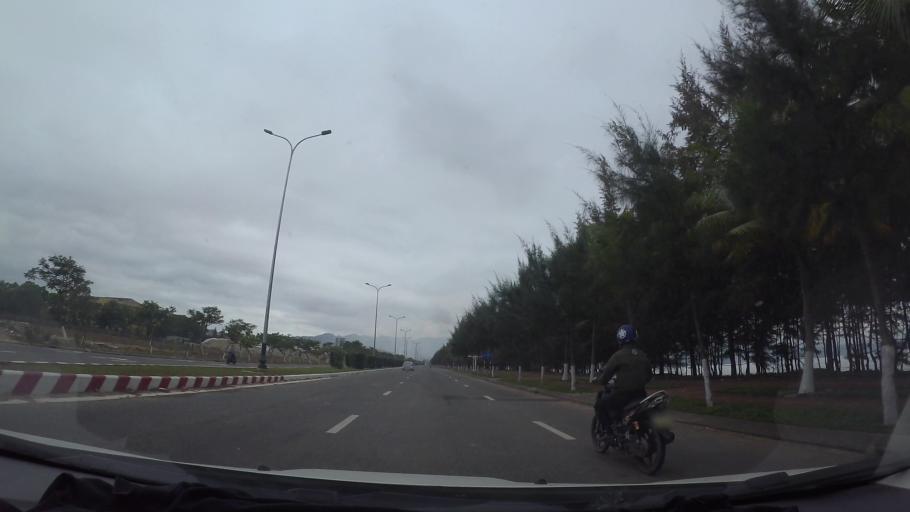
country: VN
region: Da Nang
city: Lien Chieu
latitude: 16.1025
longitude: 108.1389
